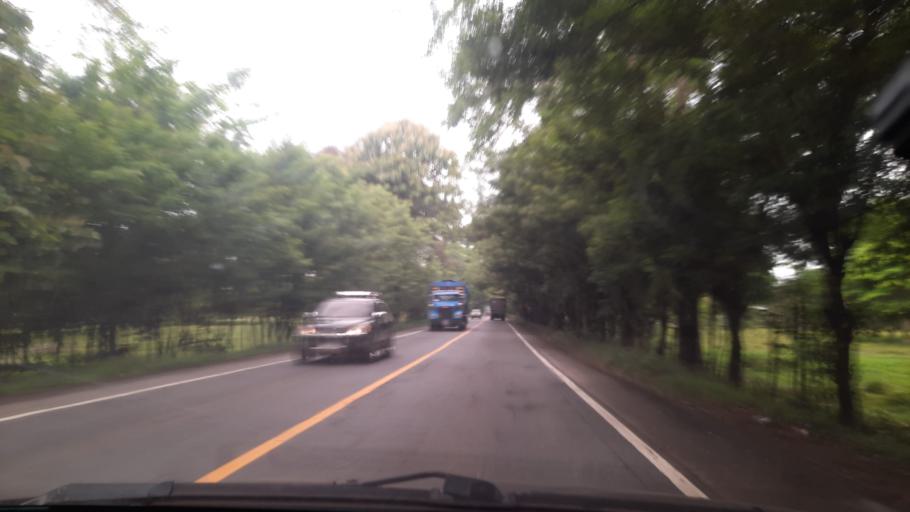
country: GT
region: Izabal
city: Morales
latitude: 15.4607
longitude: -88.9316
